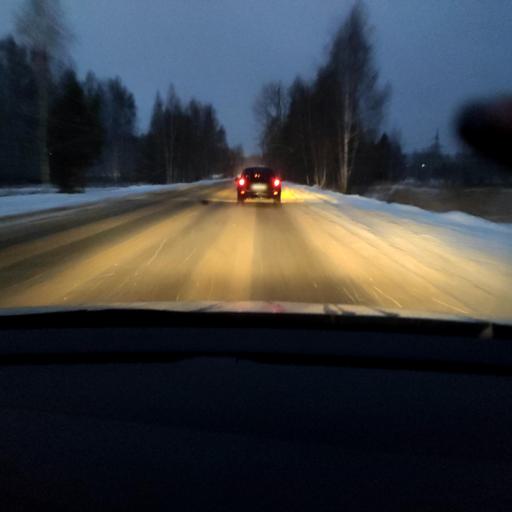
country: RU
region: Tatarstan
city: Aysha
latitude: 55.8691
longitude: 48.5804
